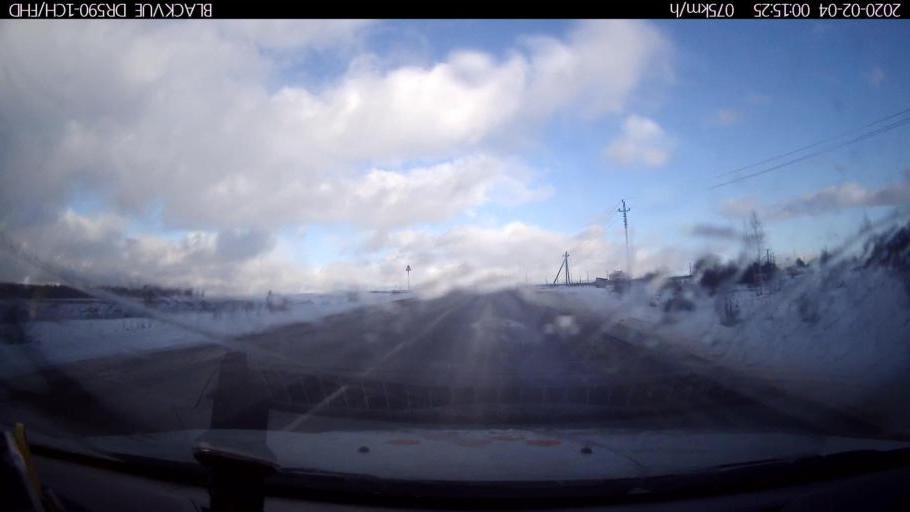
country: RU
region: Nizjnij Novgorod
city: Dal'neye Konstantinovo
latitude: 55.9304
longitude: 44.2240
